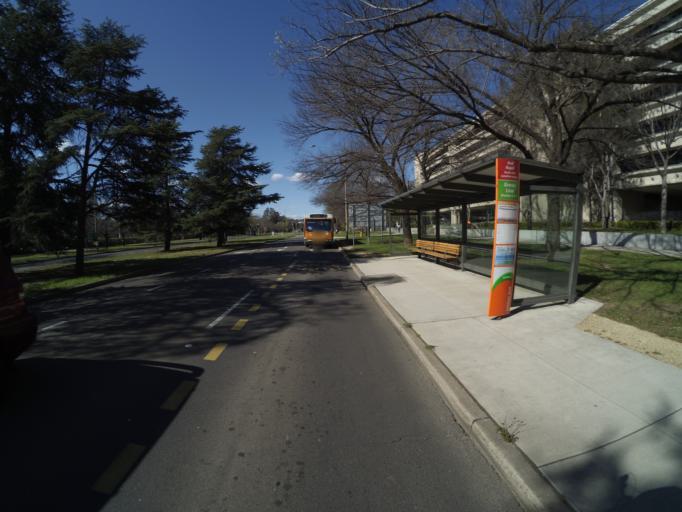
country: AU
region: Australian Capital Territory
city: Forrest
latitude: -35.3043
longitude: 149.1348
